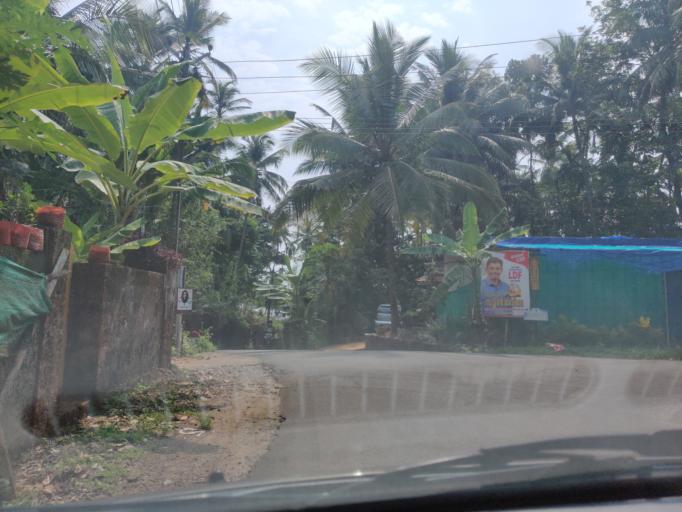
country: IN
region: Kerala
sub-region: Kozhikode
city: Kunnamangalam
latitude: 11.4185
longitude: 75.8743
